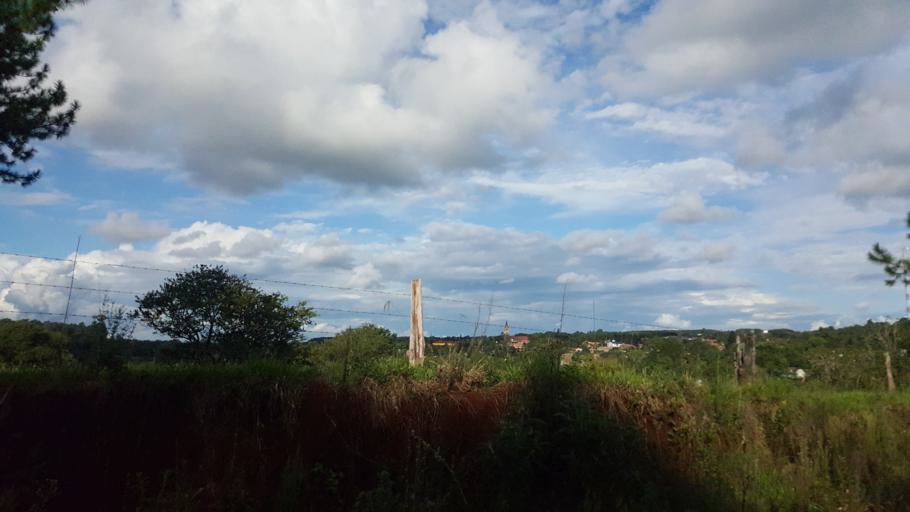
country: AR
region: Misiones
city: Capiovi
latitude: -26.9251
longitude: -55.0662
